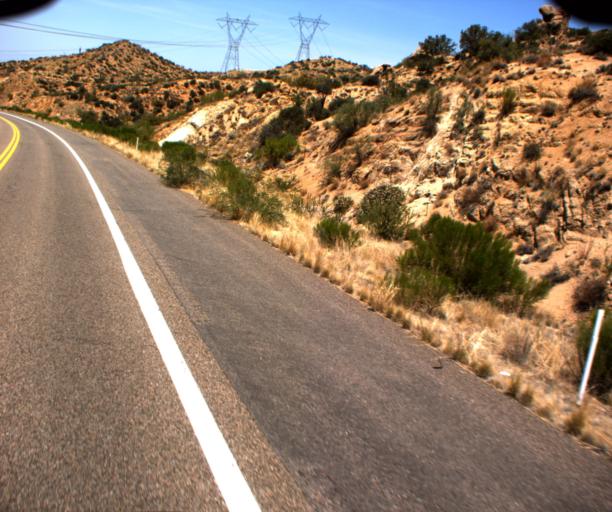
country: US
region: Arizona
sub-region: Gila County
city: Miami
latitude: 33.5440
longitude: -110.9395
